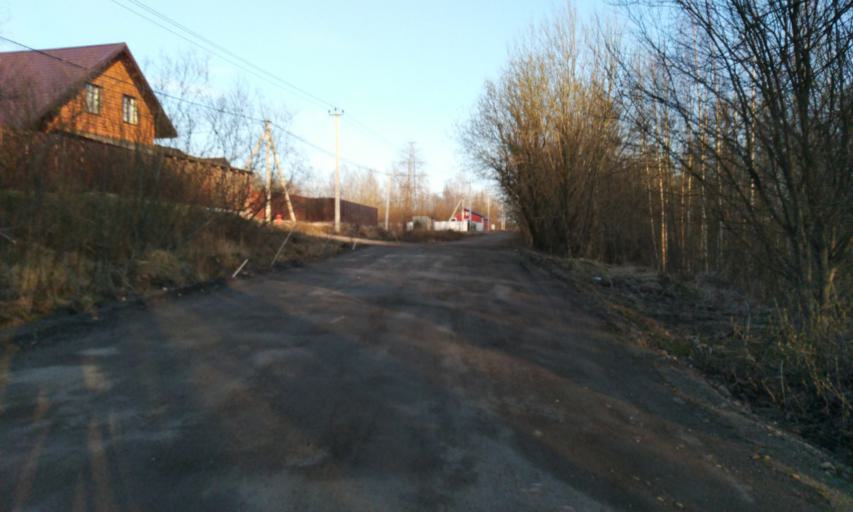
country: RU
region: Leningrad
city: Novoye Devyatkino
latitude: 60.0923
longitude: 30.4573
